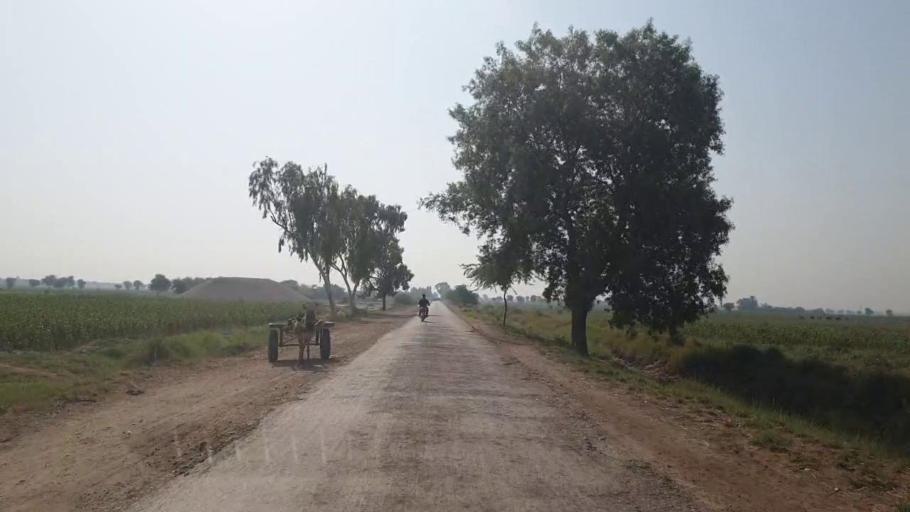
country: PK
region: Sindh
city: Shahdadpur
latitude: 25.9320
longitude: 68.7307
